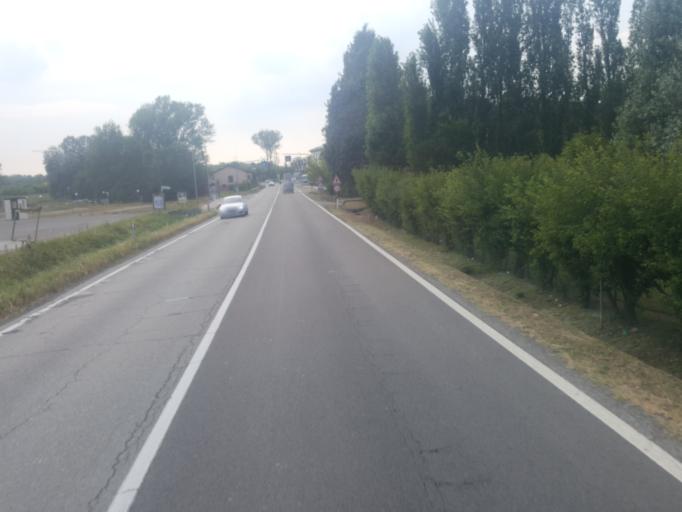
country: IT
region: Emilia-Romagna
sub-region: Provincia di Modena
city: Gaggio
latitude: 44.6225
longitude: 11.0024
